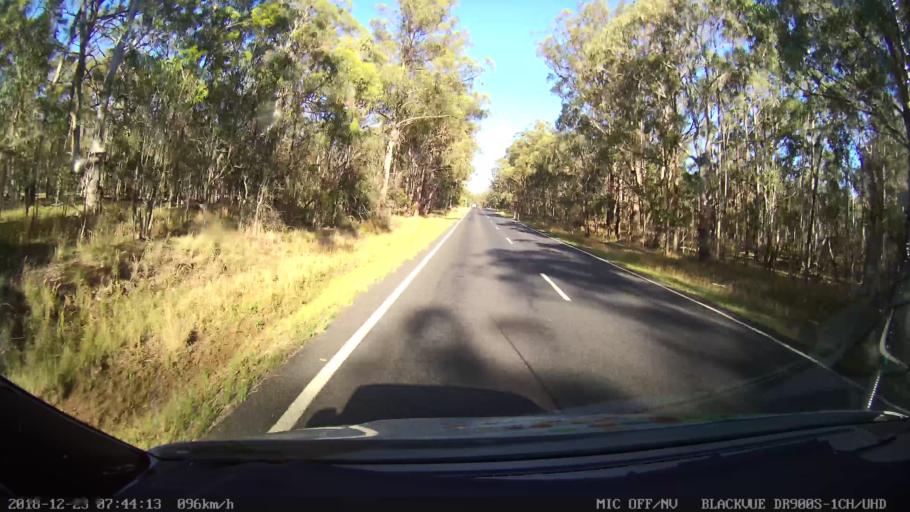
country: AU
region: New South Wales
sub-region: Armidale Dumaresq
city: Enmore
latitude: -30.5247
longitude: 151.9534
